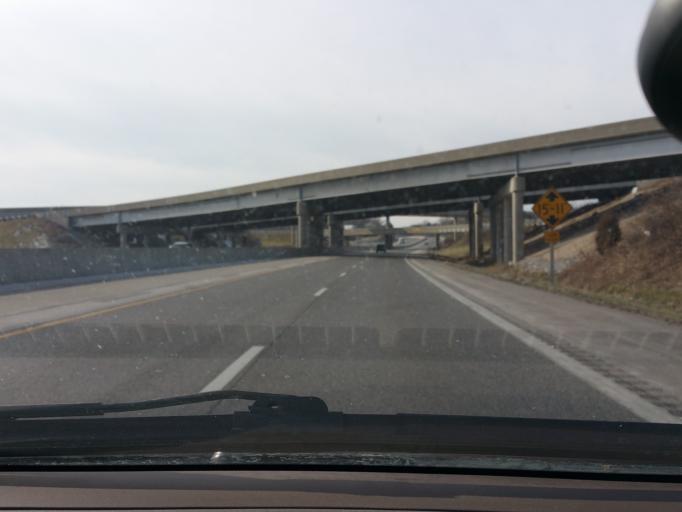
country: US
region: Missouri
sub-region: Clay County
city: Claycomo
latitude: 39.2069
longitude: -94.4904
